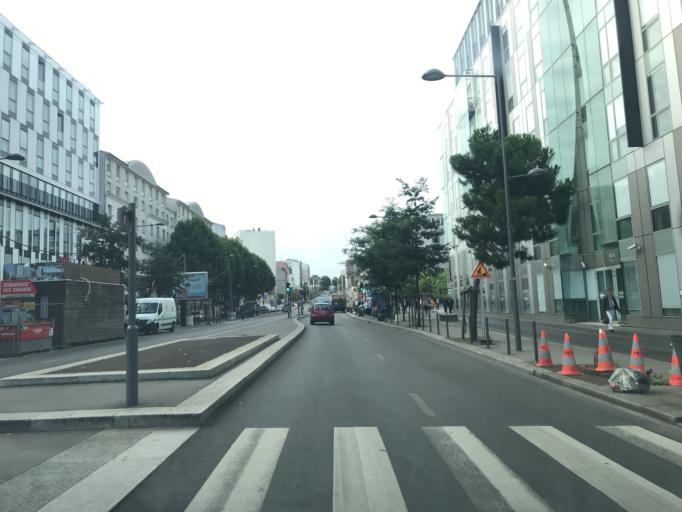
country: FR
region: Ile-de-France
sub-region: Departement du Val-de-Marne
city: Le Kremlin-Bicetre
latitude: 48.8057
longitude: 2.3635
